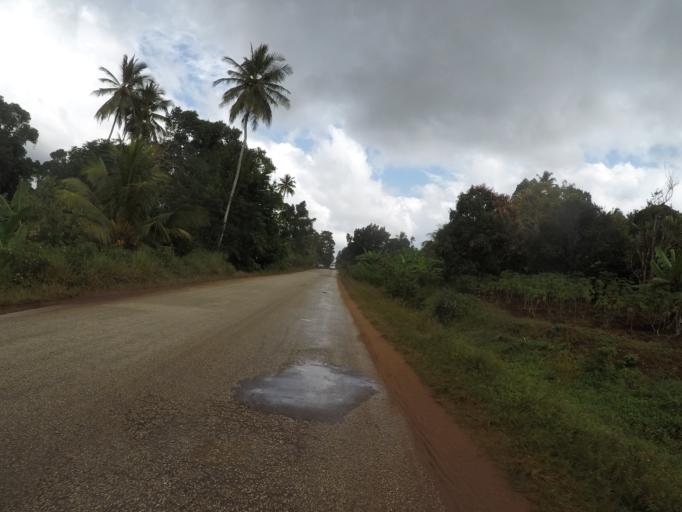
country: TZ
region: Zanzibar North
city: Gamba
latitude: -5.9375
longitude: 39.2534
